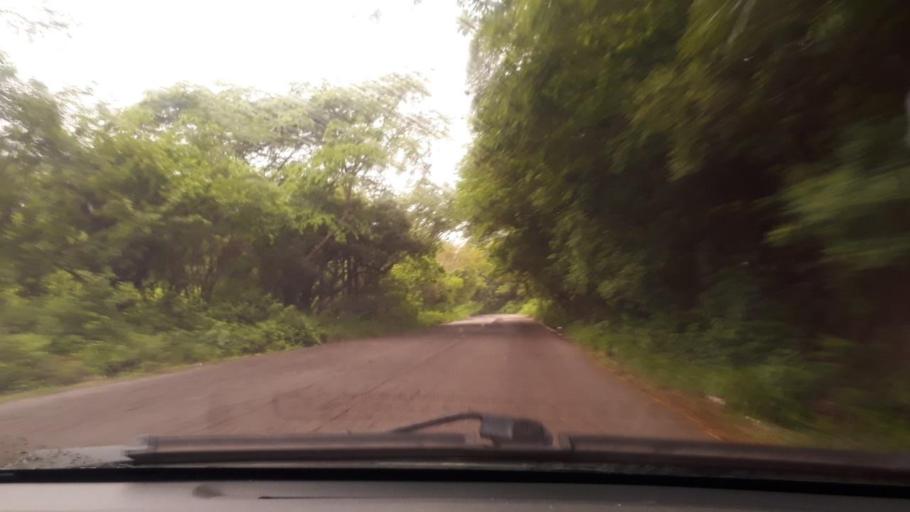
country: GT
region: Jutiapa
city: Comapa
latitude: 14.0841
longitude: -89.9585
